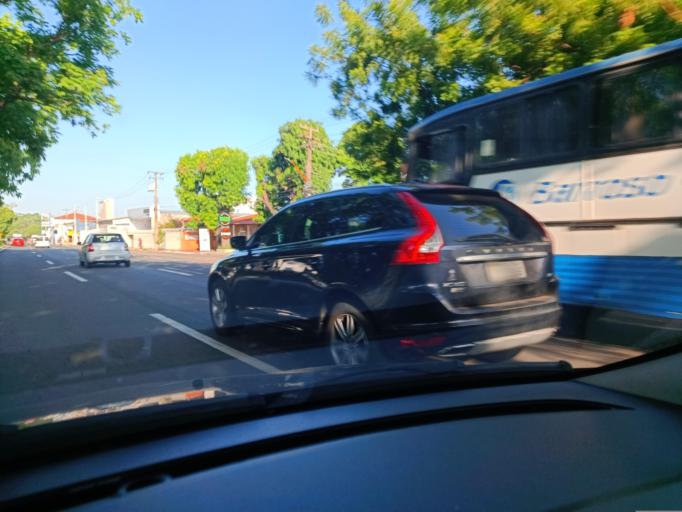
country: BR
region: Piaui
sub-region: Teresina
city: Teresina
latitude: -5.0815
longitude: -42.7718
